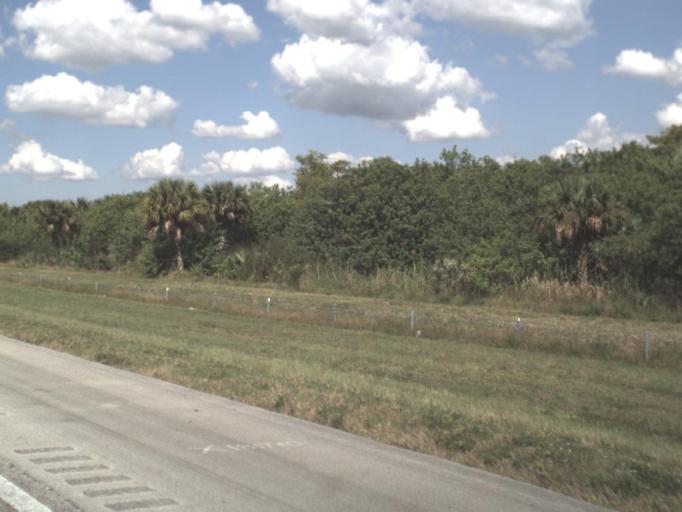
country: US
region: Florida
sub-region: Indian River County
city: West Vero Corridor
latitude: 27.5106
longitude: -80.5888
